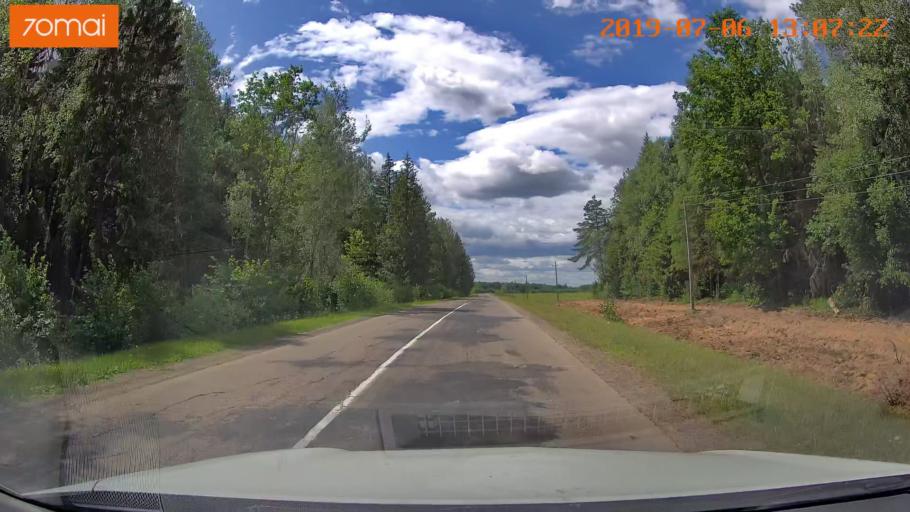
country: BY
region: Minsk
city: Enyerhyetykaw
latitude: 53.6734
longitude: 27.0418
